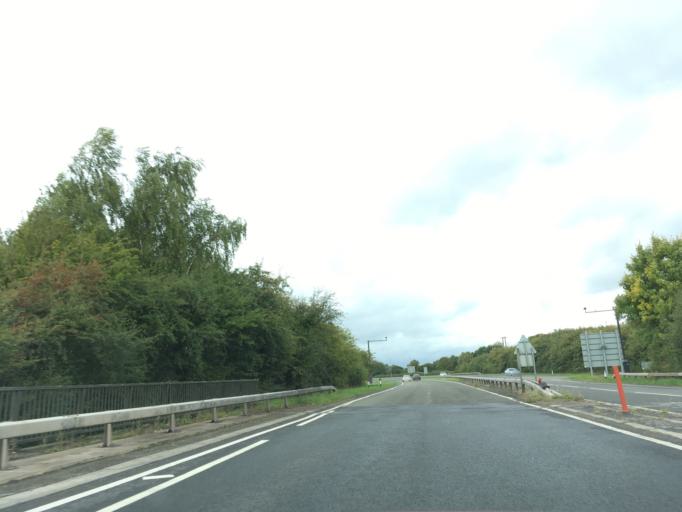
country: GB
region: Wales
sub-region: Monmouthshire
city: Llanarth
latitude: 51.7674
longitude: -2.8341
